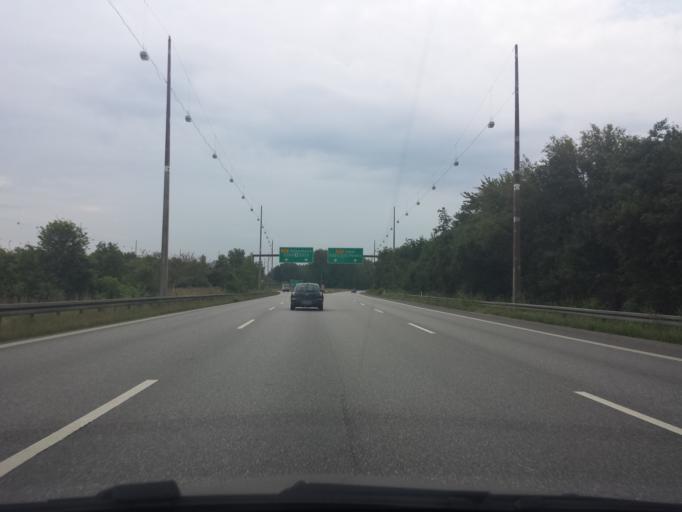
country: DK
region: Capital Region
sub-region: Albertslund Kommune
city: Albertslund
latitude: 55.6463
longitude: 12.3318
